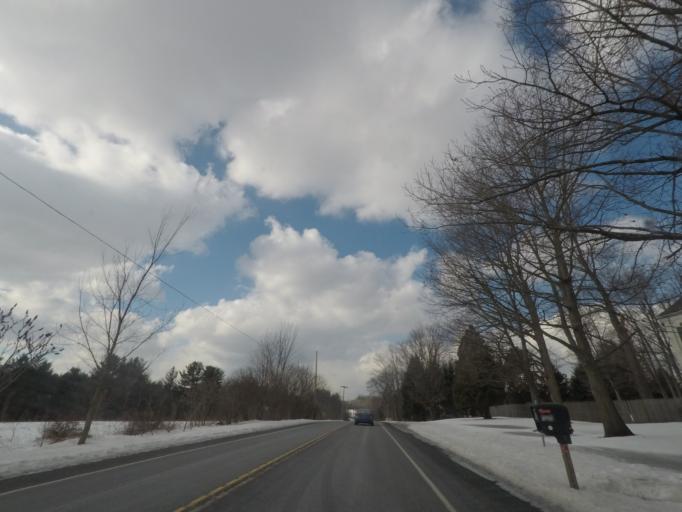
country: US
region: New York
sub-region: Saratoga County
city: Country Knolls
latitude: 42.8683
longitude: -73.8593
